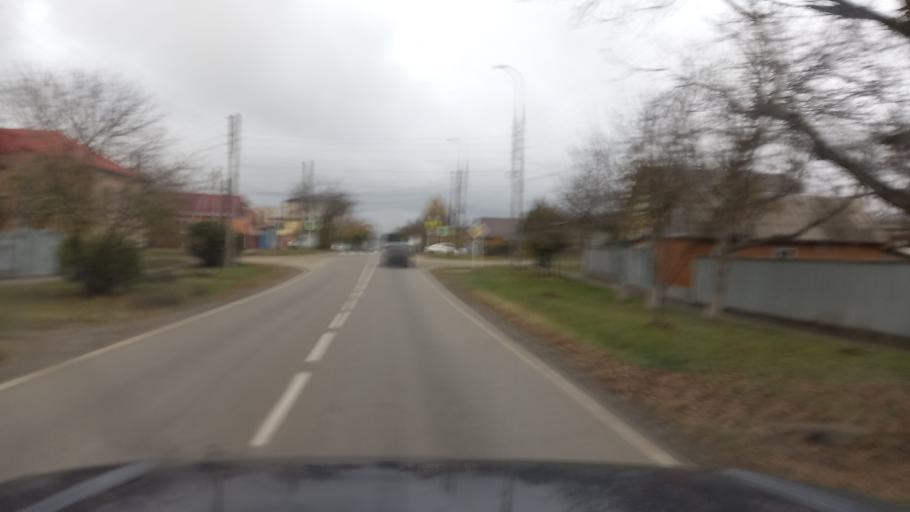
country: RU
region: Adygeya
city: Maykop
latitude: 44.6057
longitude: 40.0714
